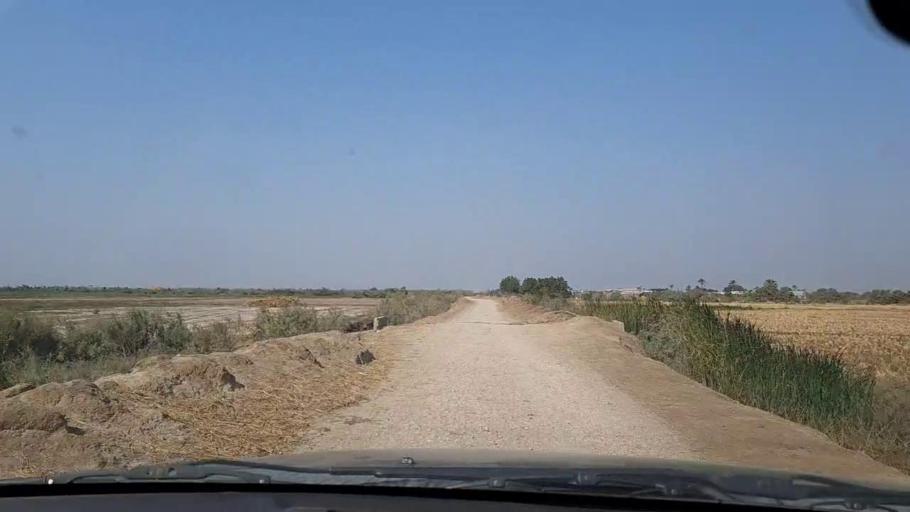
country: PK
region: Sindh
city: Mirpur Sakro
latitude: 24.3577
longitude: 67.6831
